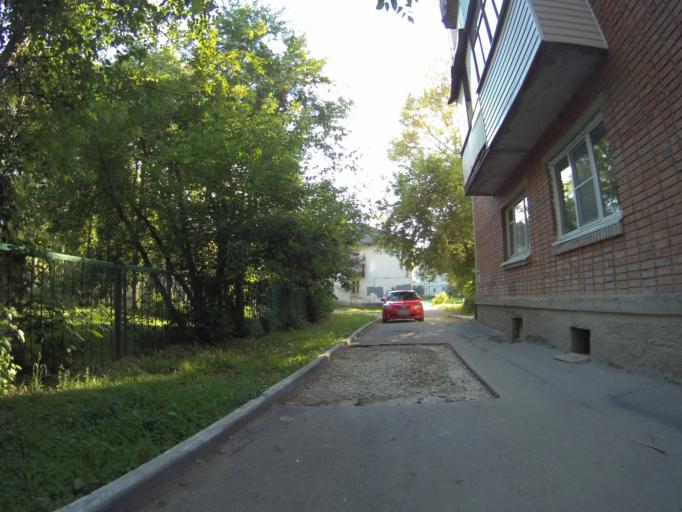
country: RU
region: Vladimir
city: Raduzhnyy
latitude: 56.1007
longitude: 40.2816
